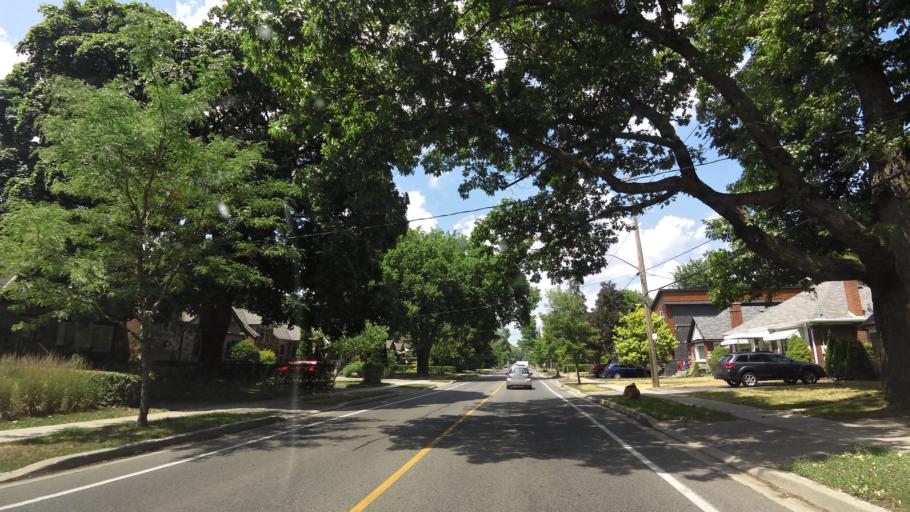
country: CA
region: Ontario
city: Etobicoke
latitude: 43.6444
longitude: -79.5101
